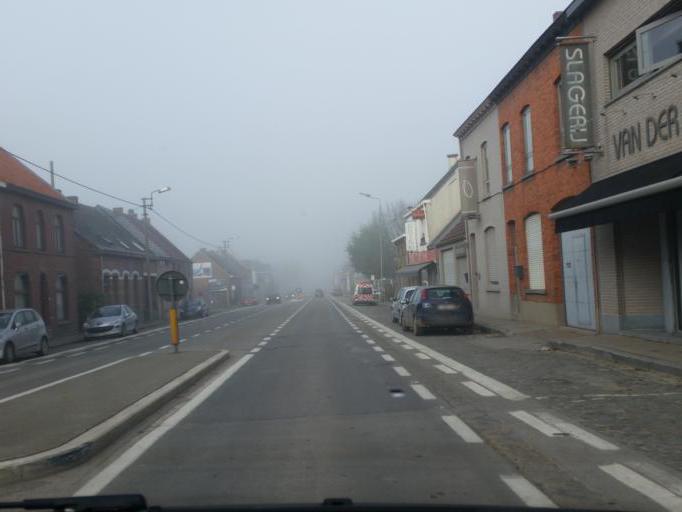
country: BE
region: Flanders
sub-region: Provincie Oost-Vlaanderen
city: Wetteren
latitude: 50.9583
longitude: 3.8983
